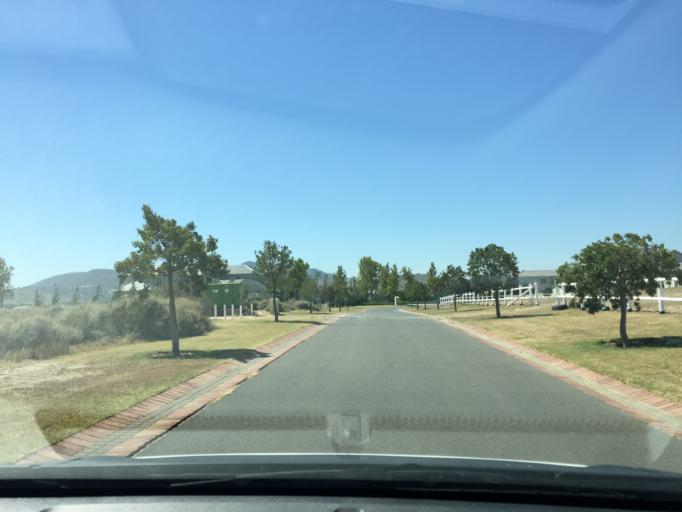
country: ZA
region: Western Cape
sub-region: Cape Winelands District Municipality
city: Paarl
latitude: -33.8069
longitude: 18.9768
